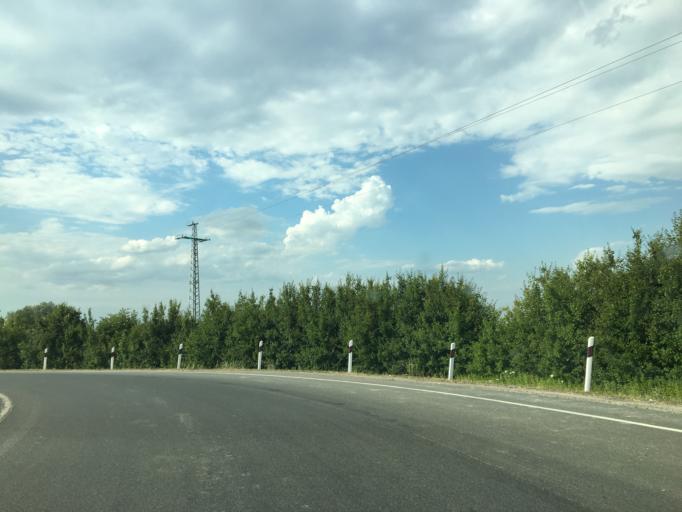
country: HU
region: Bacs-Kiskun
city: Dusnok
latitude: 46.3543
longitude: 18.9658
